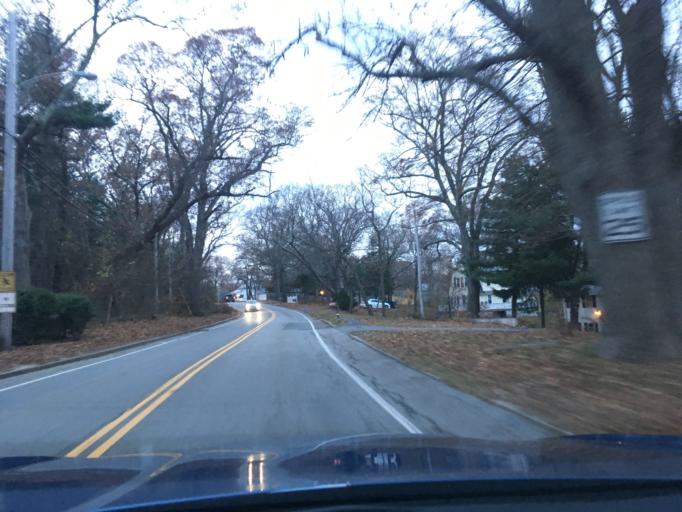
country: US
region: Rhode Island
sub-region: Kent County
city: East Greenwich
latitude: 41.6856
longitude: -71.4577
